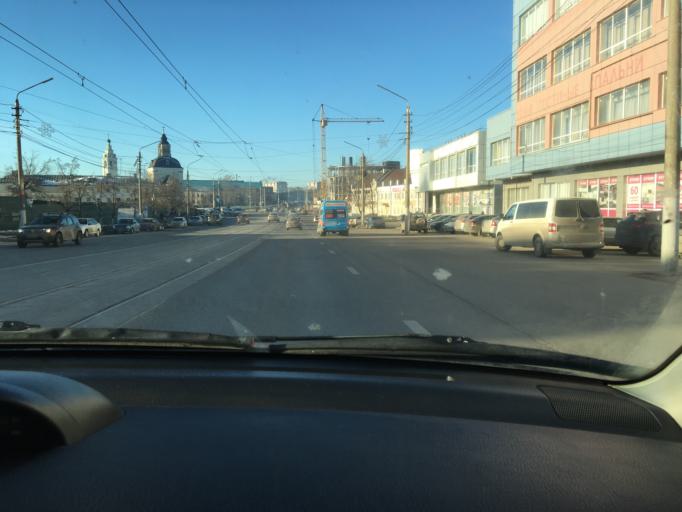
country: RU
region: Tula
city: Tula
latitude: 54.2040
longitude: 37.6211
